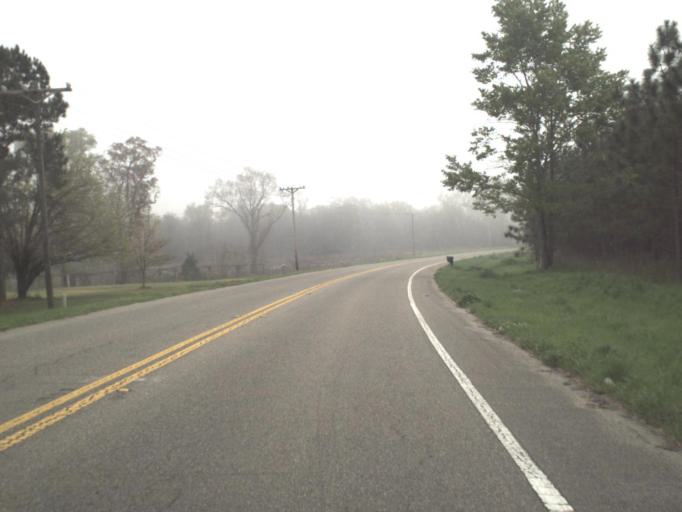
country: US
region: Florida
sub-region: Gadsden County
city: Gretna
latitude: 30.5359
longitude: -84.6836
